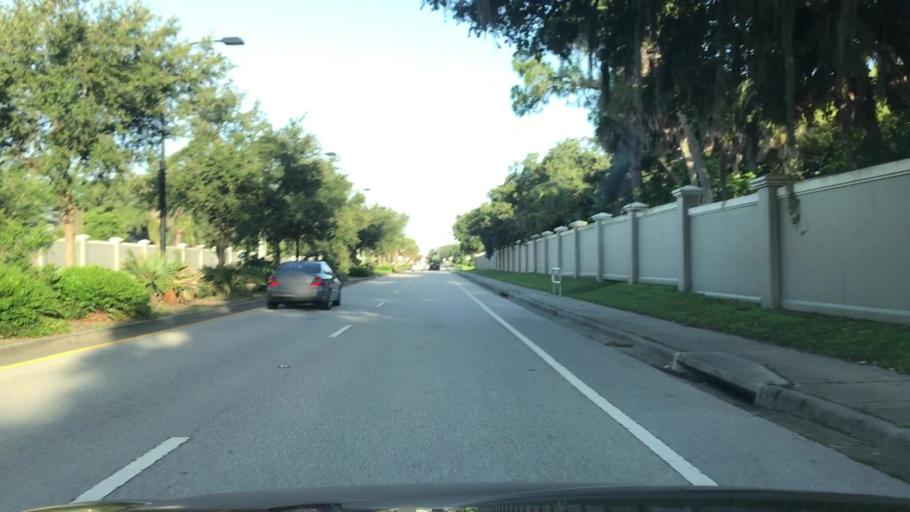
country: US
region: Florida
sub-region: Sarasota County
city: Sarasota Springs
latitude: 27.3230
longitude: -82.4781
